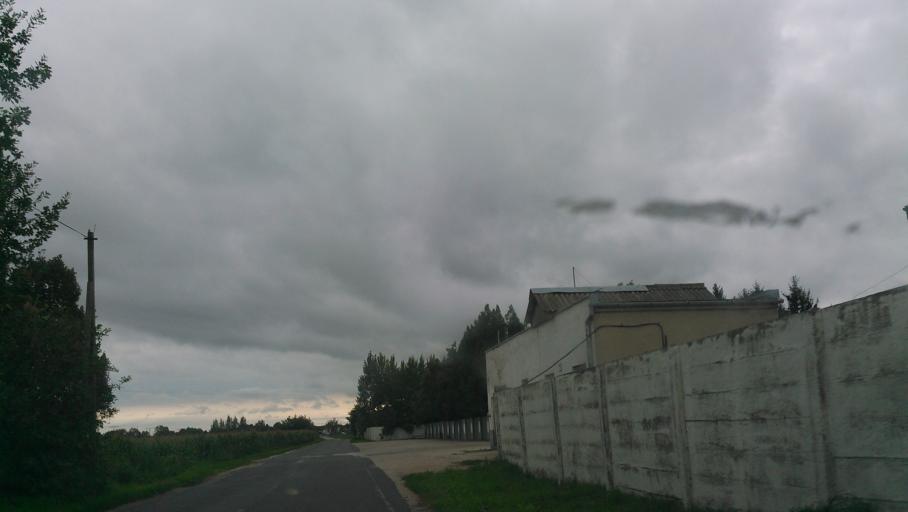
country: SK
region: Trnavsky
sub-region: Okres Dunajska Streda
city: Velky Meder
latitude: 47.9321
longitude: 17.7263
